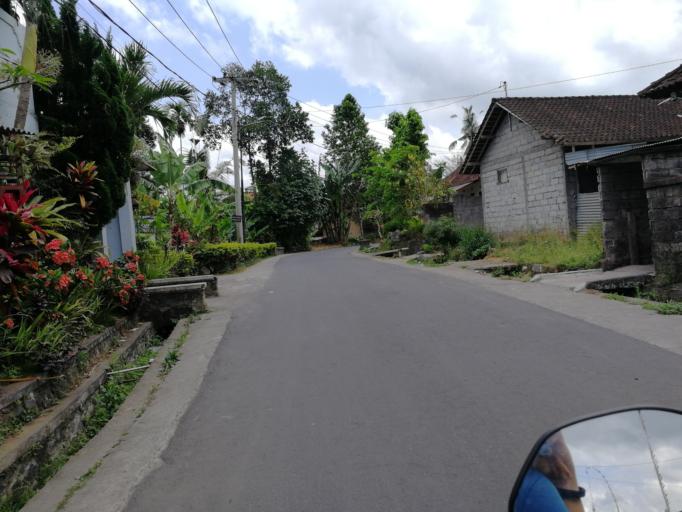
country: ID
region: Bali
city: Banjar Wangsian
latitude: -8.4685
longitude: 115.4445
